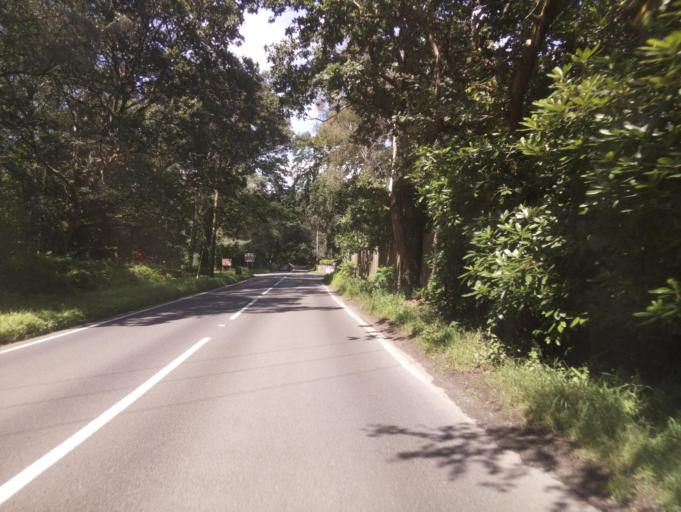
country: GB
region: England
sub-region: West Berkshire
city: Winterbourne
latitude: 51.4358
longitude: -1.3336
